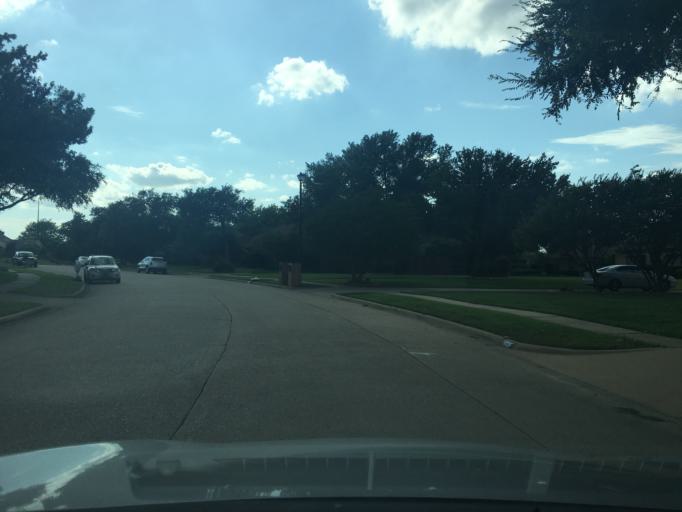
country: US
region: Texas
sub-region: Dallas County
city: Garland
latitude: 32.9402
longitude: -96.6787
